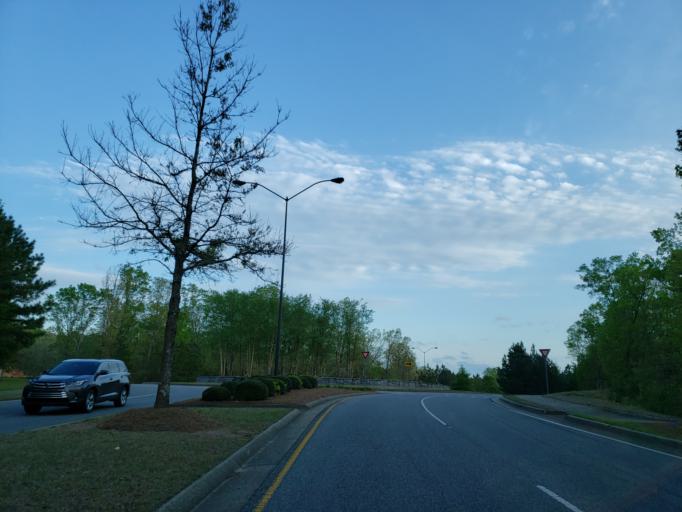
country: US
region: Georgia
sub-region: Cherokee County
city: Canton
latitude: 34.2804
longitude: -84.4688
